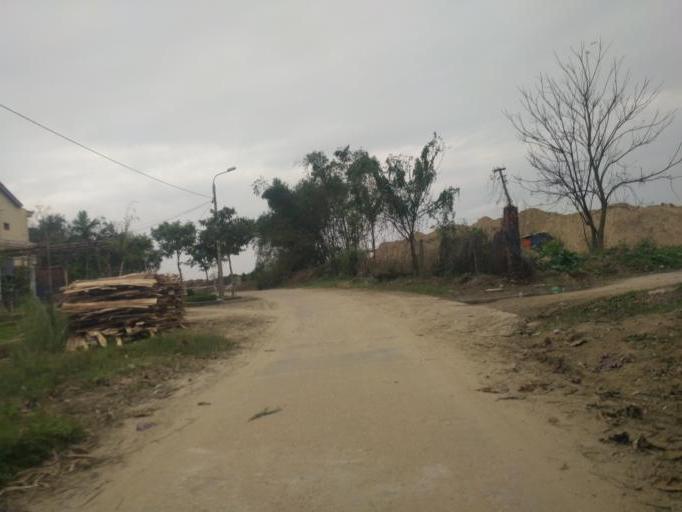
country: VN
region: Quang Nam
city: Hoi An
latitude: 15.8728
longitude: 108.3296
